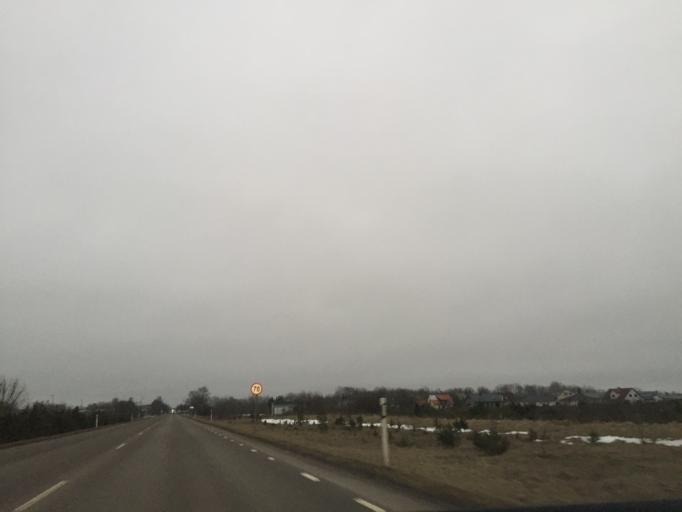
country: EE
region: Saare
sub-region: Kuressaare linn
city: Kuressaare
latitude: 58.2474
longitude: 22.5060
